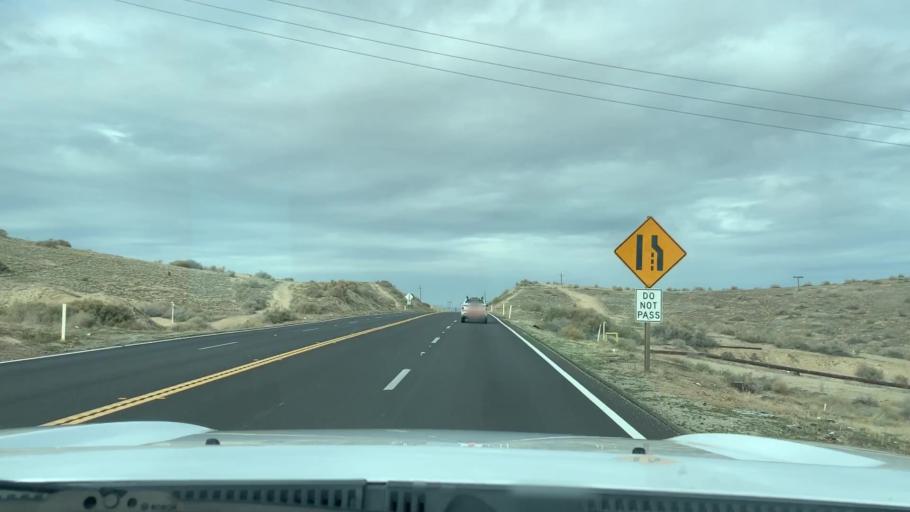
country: US
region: California
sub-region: Kern County
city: South Taft
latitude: 35.1189
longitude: -119.4331
